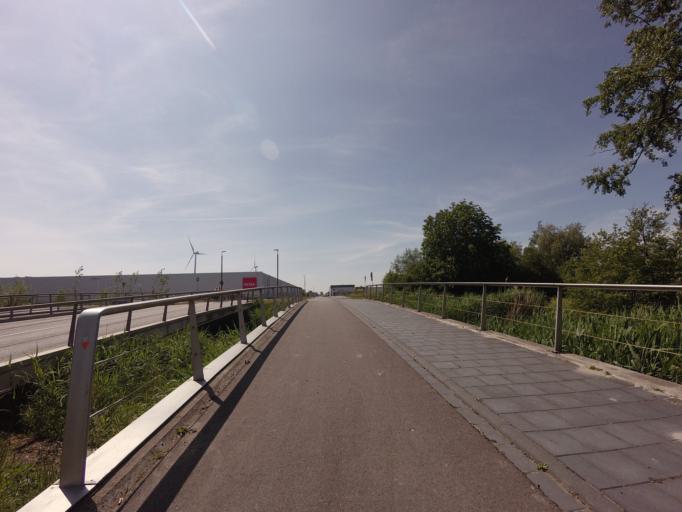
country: NL
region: Utrecht
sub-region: Gemeente Vianen
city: Vianen
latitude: 52.0199
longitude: 5.1172
